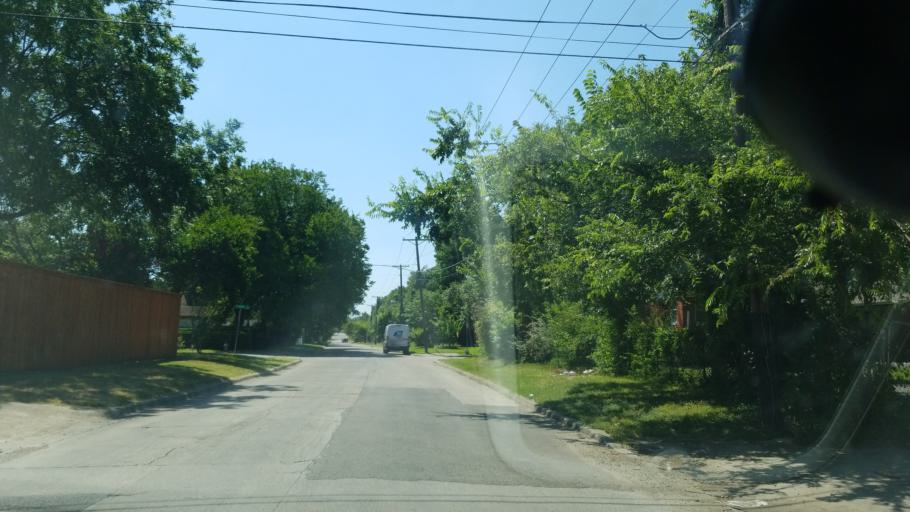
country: US
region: Texas
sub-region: Dallas County
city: Cockrell Hill
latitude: 32.7171
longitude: -96.8354
